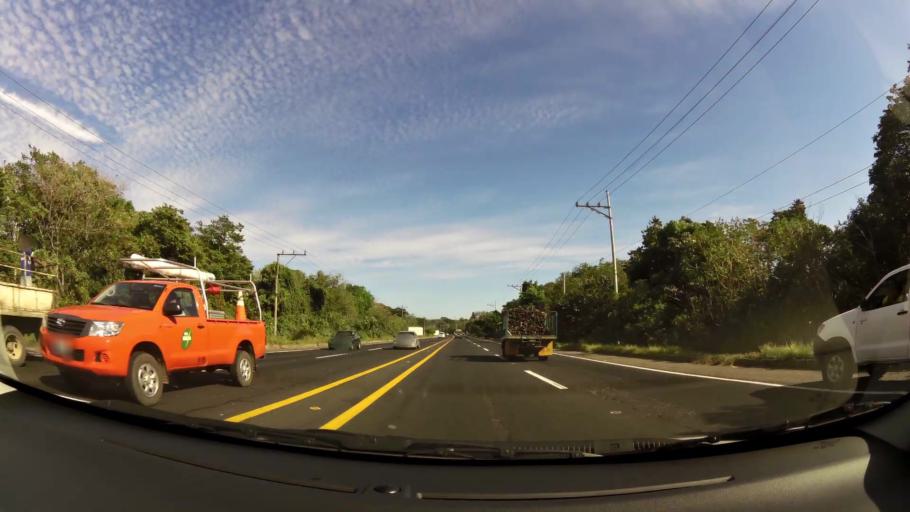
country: SV
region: Santa Ana
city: Santa Ana
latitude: 13.9870
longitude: -89.6060
